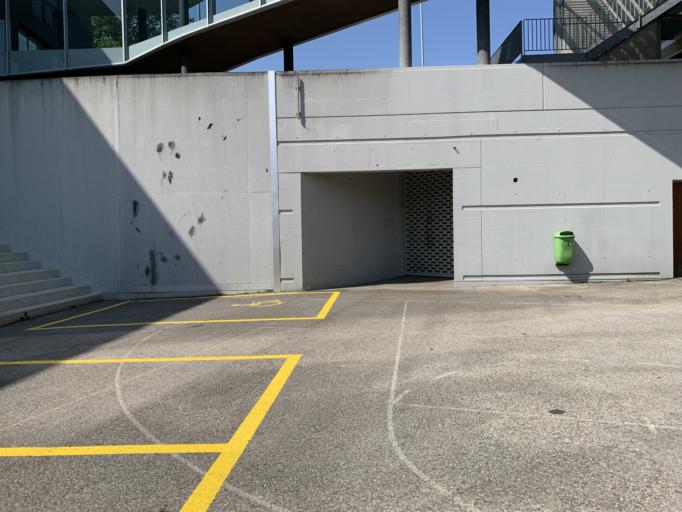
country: CH
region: Vaud
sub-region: Nyon District
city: Genolier
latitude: 46.4334
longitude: 6.2214
